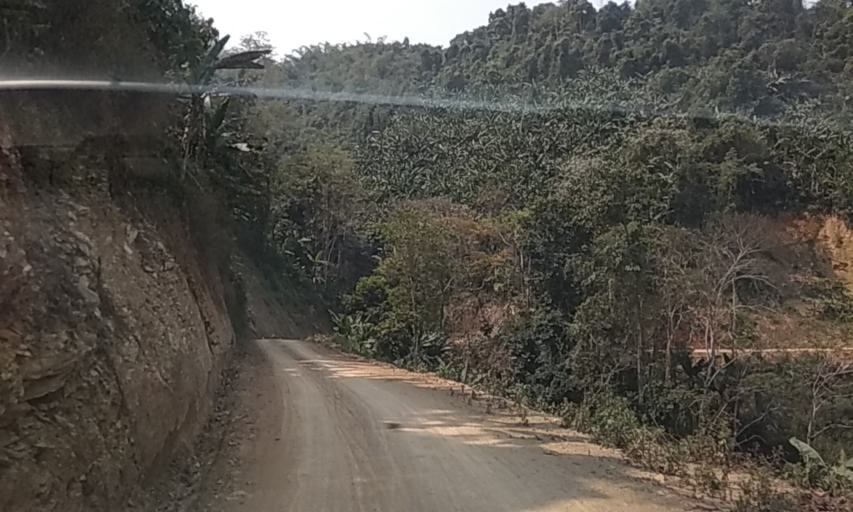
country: LA
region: Phongsali
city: Phongsali
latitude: 21.4637
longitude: 102.4239
